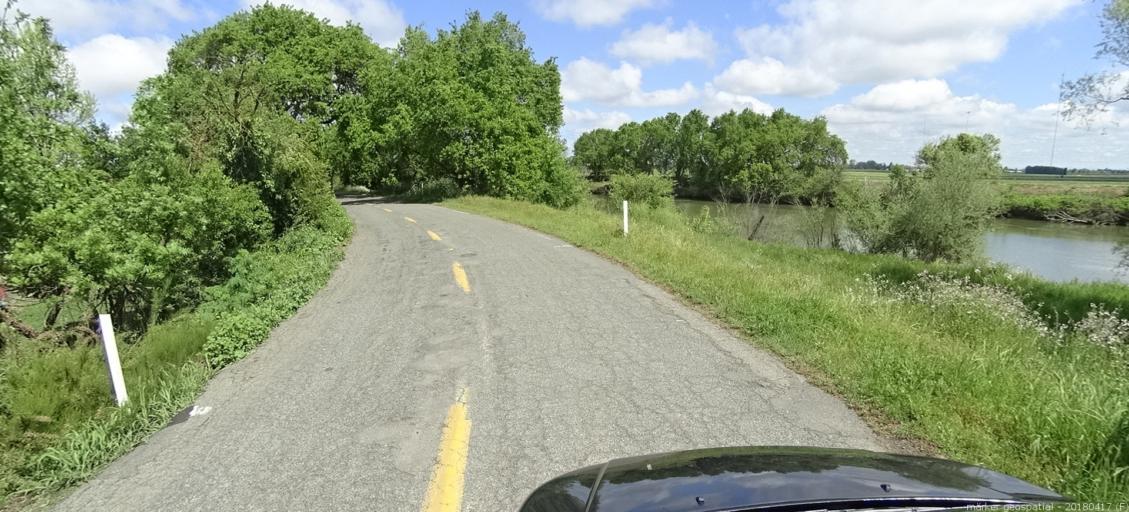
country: US
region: California
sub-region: Sacramento County
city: Walnut Grove
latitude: 38.2117
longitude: -121.5369
